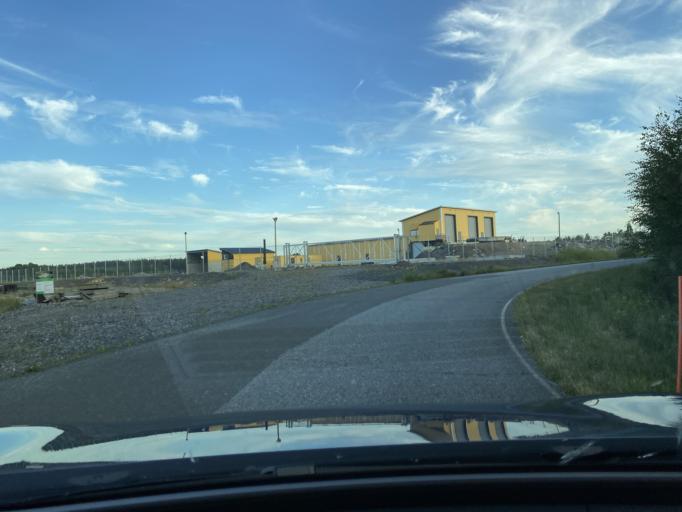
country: FI
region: Pirkanmaa
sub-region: Lounais-Pirkanmaa
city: Punkalaidun
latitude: 61.0411
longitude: 22.9998
